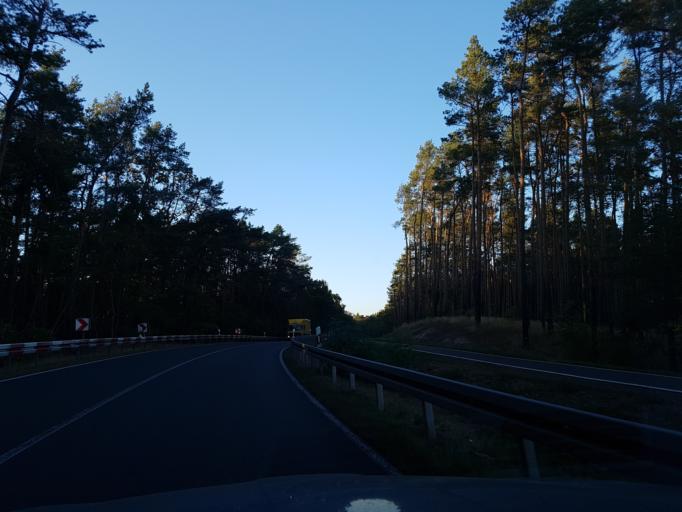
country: DE
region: Brandenburg
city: Schilda
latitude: 51.5642
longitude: 13.3640
